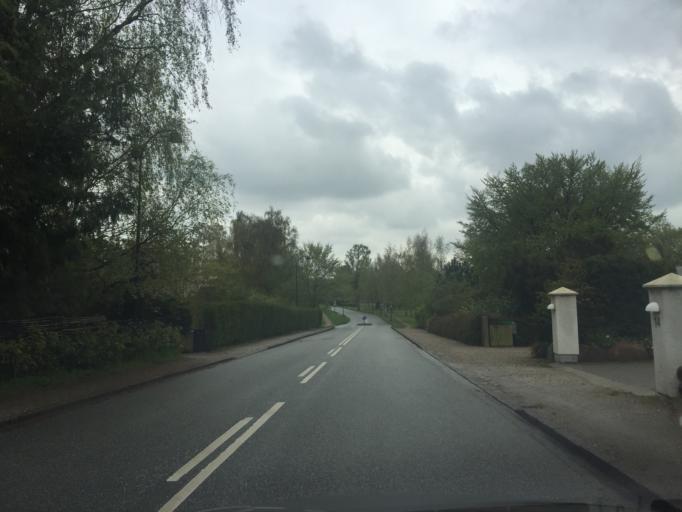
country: DK
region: Capital Region
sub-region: Rudersdal Kommune
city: Holte
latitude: 55.8060
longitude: 12.4492
